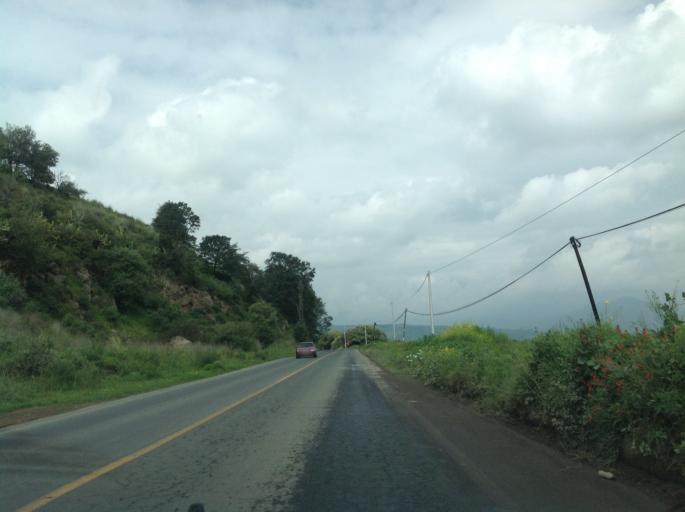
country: MX
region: Mexico
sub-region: Tenango del Valle
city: Santa Maria Jajalpa
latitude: 19.1171
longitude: -99.5572
